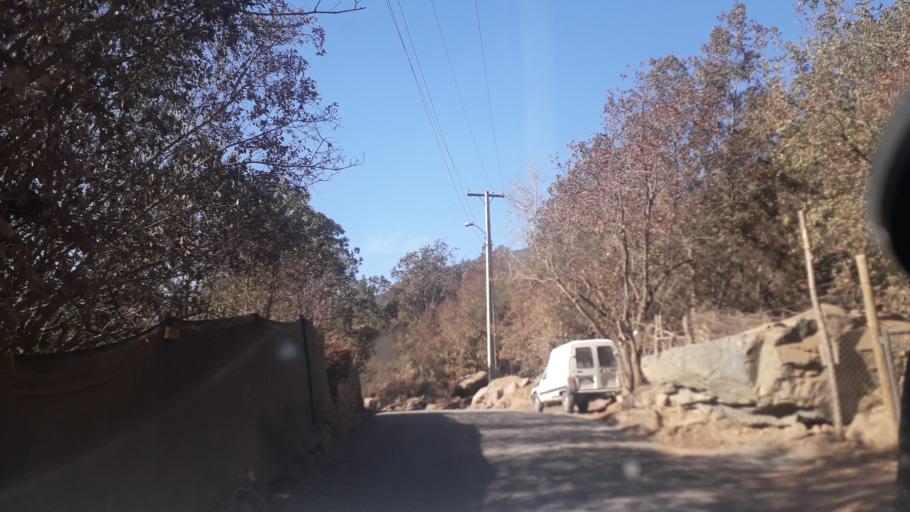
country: CL
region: Valparaiso
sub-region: Provincia de Marga Marga
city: Limache
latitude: -33.0776
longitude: -71.1000
